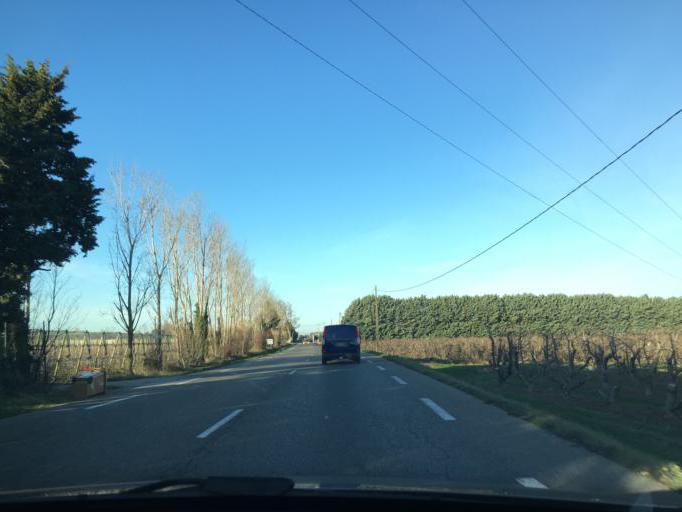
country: FR
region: Provence-Alpes-Cote d'Azur
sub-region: Departement du Vaucluse
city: Caumont-sur-Durance
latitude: 43.8843
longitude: 4.9914
